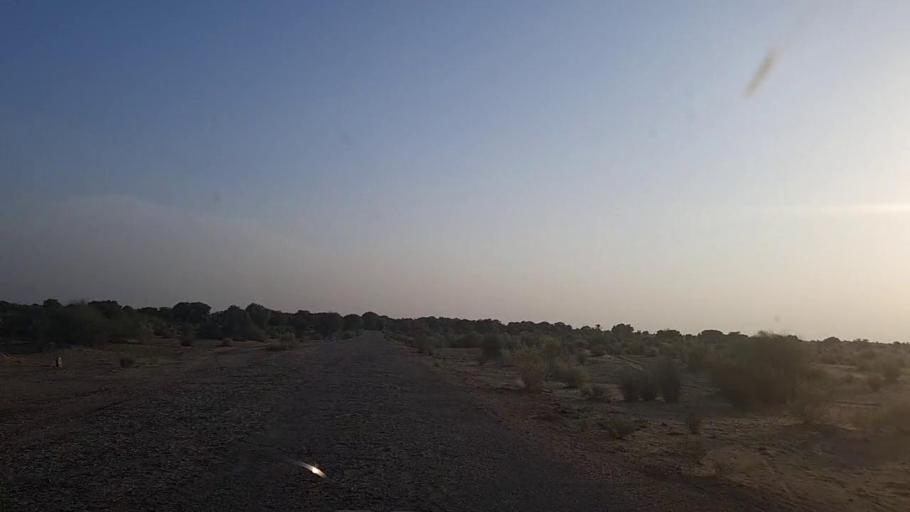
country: PK
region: Sindh
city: Khanpur
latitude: 27.6381
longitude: 69.4511
